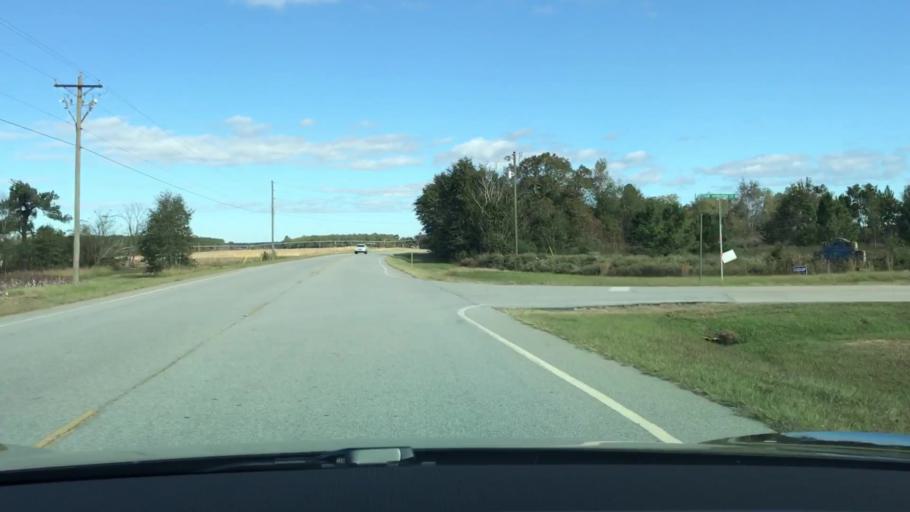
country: US
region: Georgia
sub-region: Jefferson County
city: Wrens
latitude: 33.1489
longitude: -82.4572
